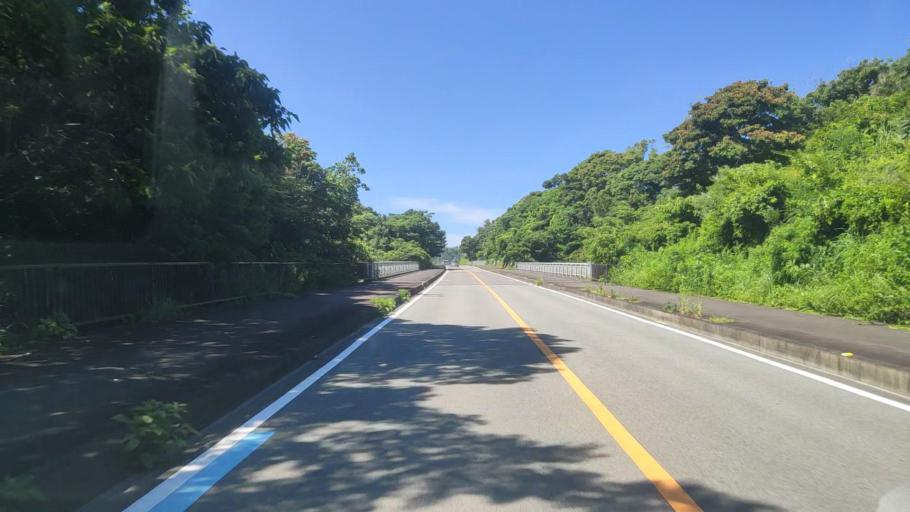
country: JP
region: Wakayama
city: Shingu
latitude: 33.7098
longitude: 135.9968
